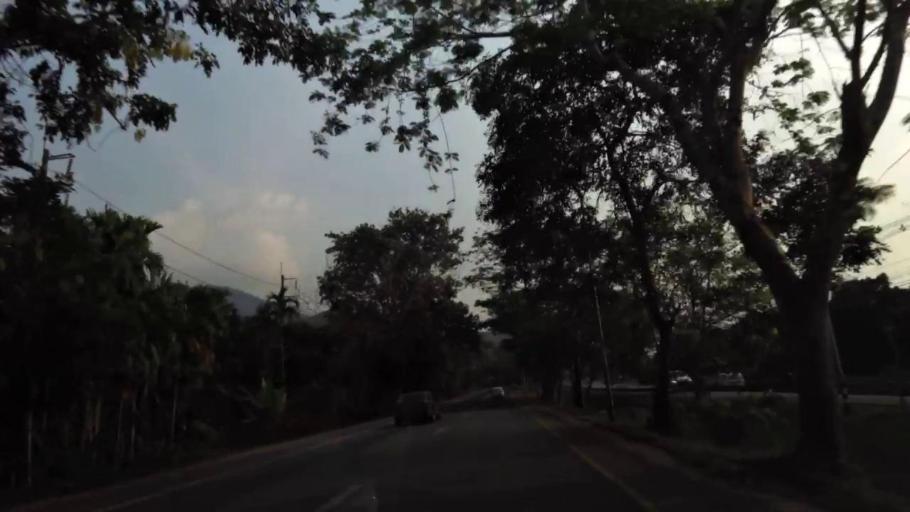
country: TH
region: Chanthaburi
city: Chanthaburi
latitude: 12.5722
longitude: 102.1624
